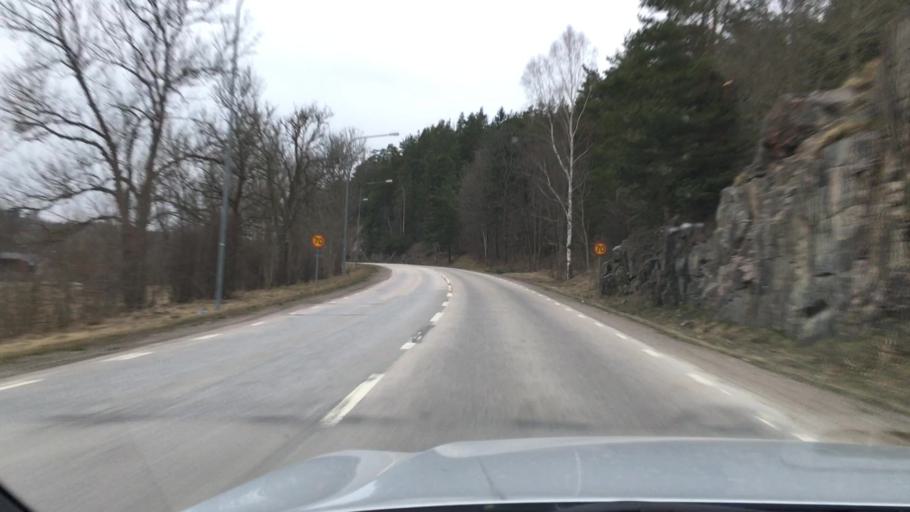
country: SE
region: OEstergoetland
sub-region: Valdemarsviks Kommun
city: Valdemarsvik
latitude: 58.2128
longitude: 16.5837
